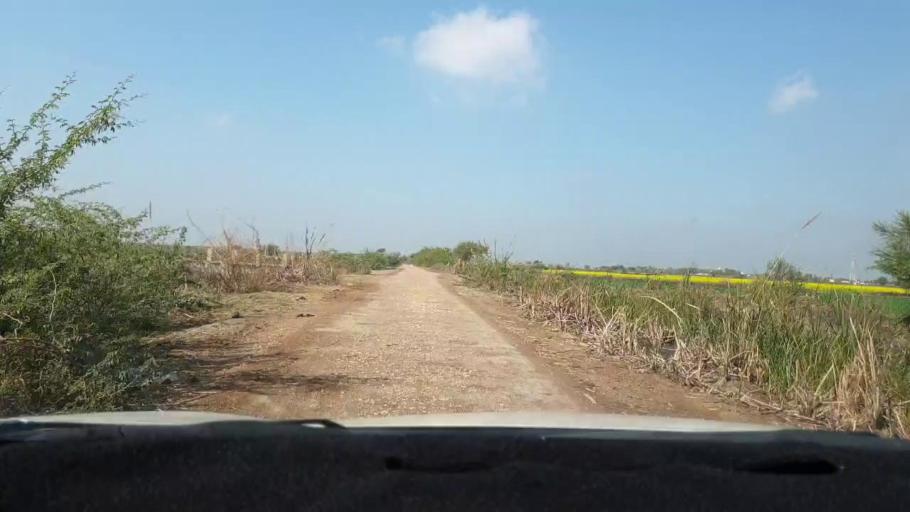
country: PK
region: Sindh
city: Berani
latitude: 25.7673
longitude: 68.8619
